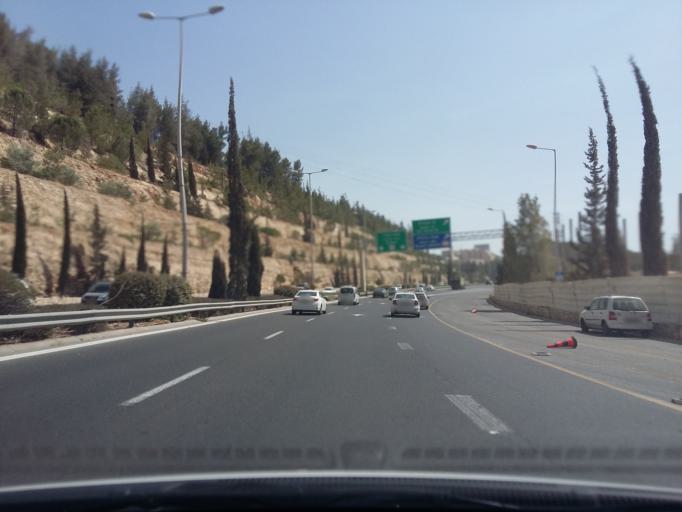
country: IL
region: Jerusalem
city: West Jerusalem
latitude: 31.8126
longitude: 35.2117
